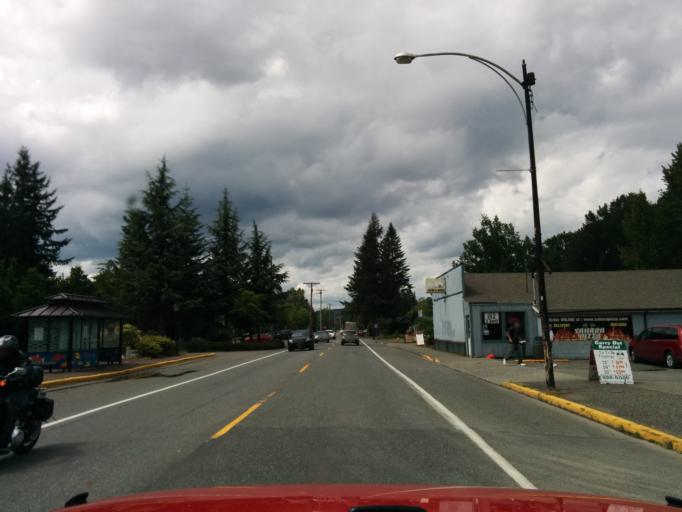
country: US
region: Washington
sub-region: King County
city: Snoqualmie
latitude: 47.5291
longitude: -121.8256
